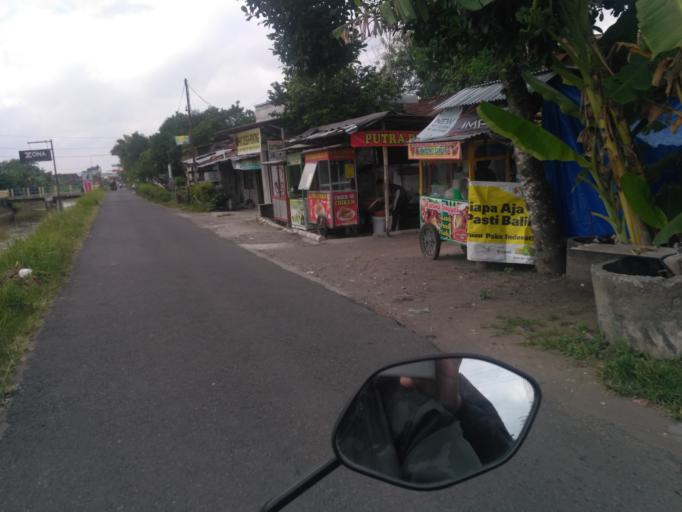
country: ID
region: Daerah Istimewa Yogyakarta
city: Yogyakarta
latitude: -7.7583
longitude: 110.3583
